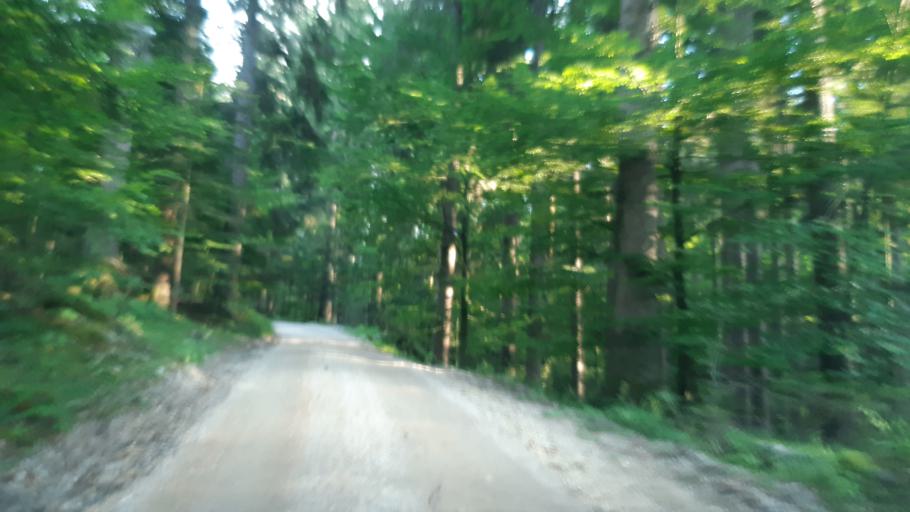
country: SI
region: Dolenjske Toplice
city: Dolenjske Toplice
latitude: 45.6976
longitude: 15.0108
